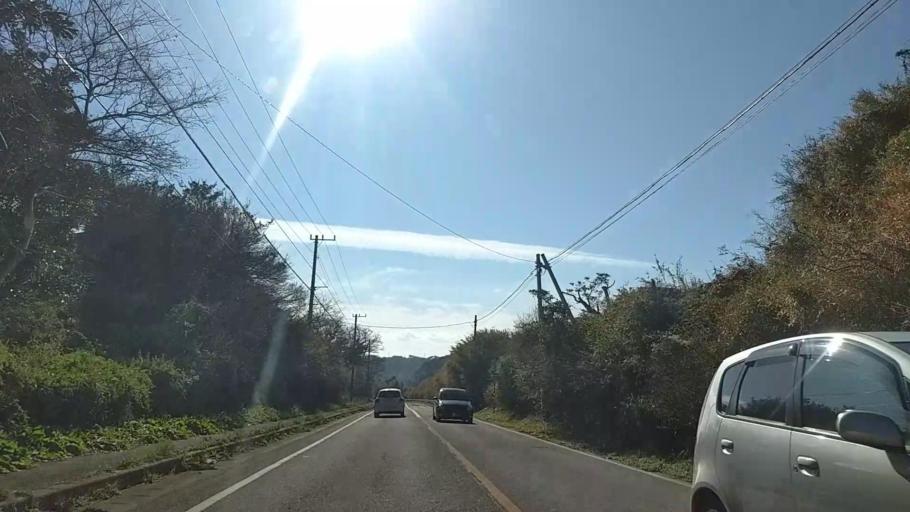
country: JP
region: Chiba
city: Asahi
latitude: 35.7058
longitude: 140.7406
